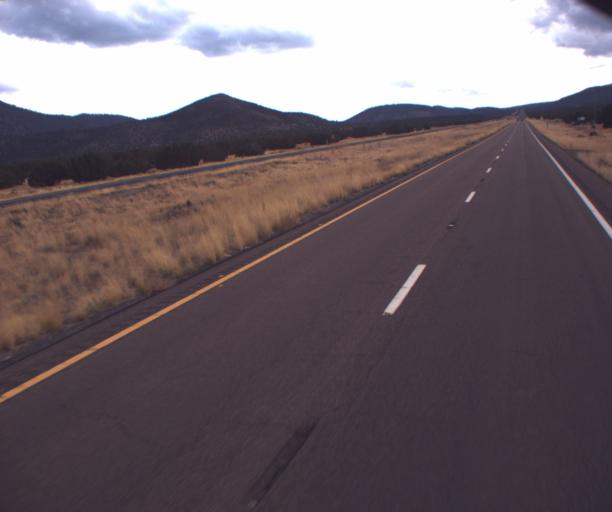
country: US
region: Arizona
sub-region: Coconino County
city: Flagstaff
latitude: 35.4376
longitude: -111.5667
